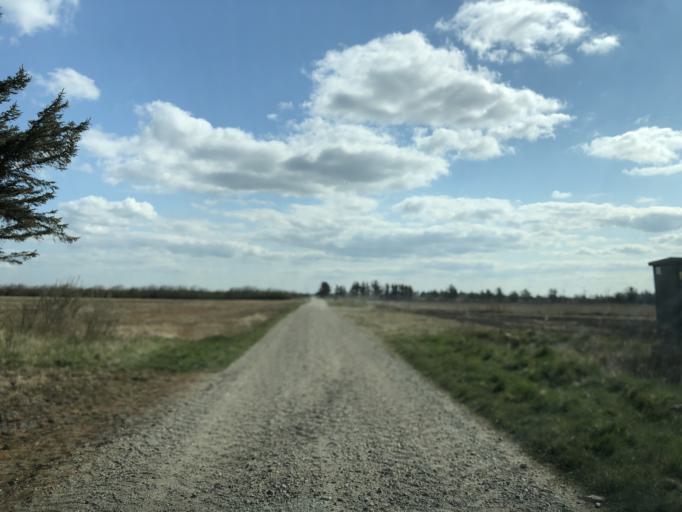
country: DK
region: Central Jutland
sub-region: Holstebro Kommune
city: Ulfborg
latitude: 56.4024
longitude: 8.1865
